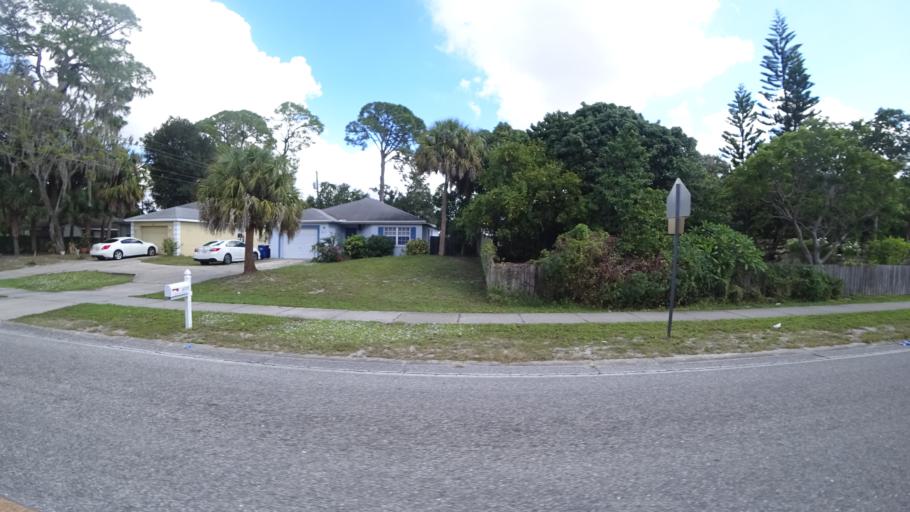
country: US
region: Florida
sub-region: Manatee County
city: Whitfield
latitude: 27.4251
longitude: -82.5550
